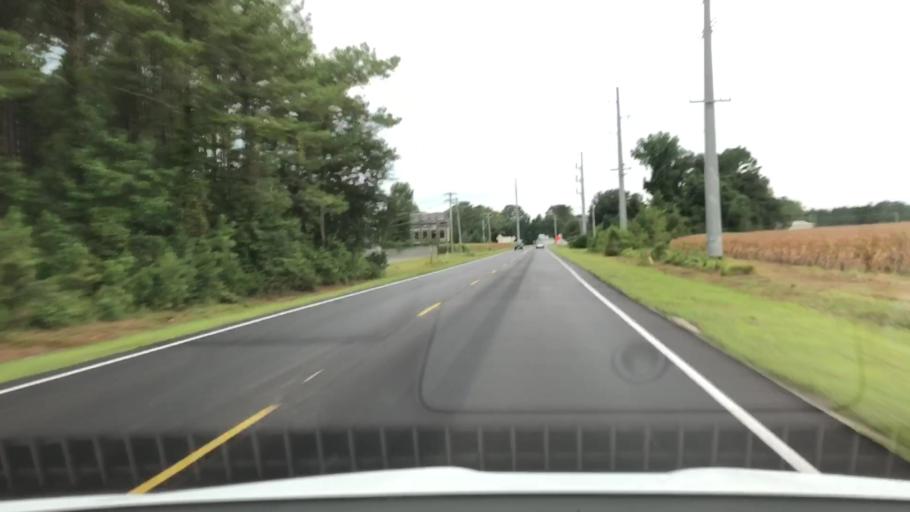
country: US
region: North Carolina
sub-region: Onslow County
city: Swansboro
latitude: 34.7885
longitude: -77.1251
